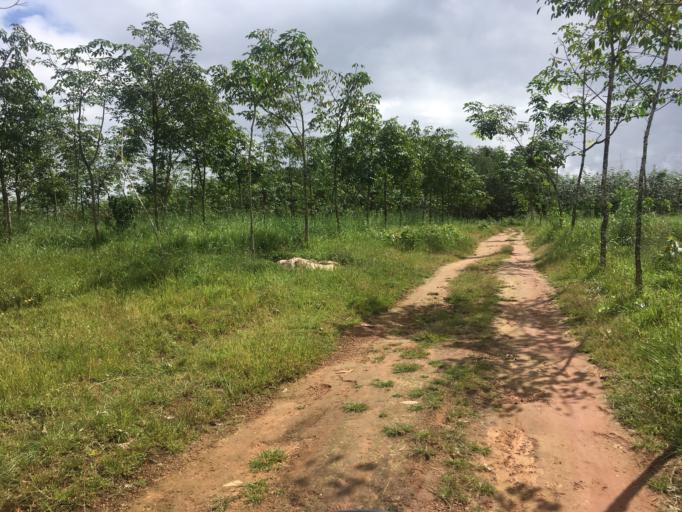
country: MM
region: Mon
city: Mawlamyine
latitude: 16.4623
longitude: 97.6889
